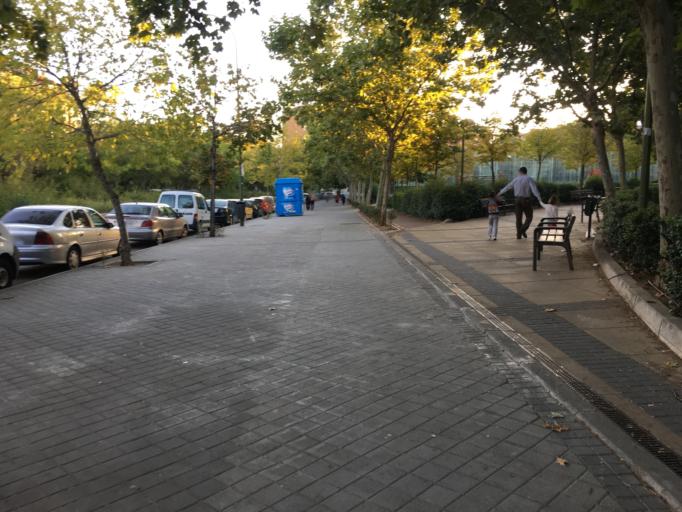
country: ES
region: Madrid
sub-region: Provincia de Madrid
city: Moratalaz
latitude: 40.4303
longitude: -3.6401
